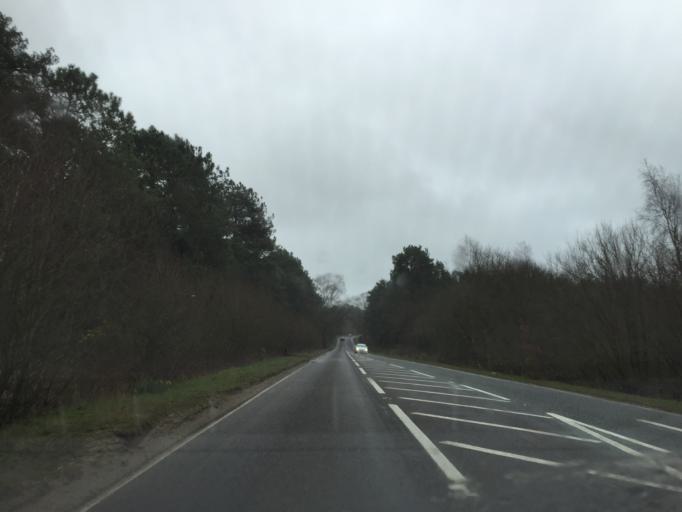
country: GB
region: England
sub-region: Dorset
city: Verwood
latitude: 50.8663
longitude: -1.8407
